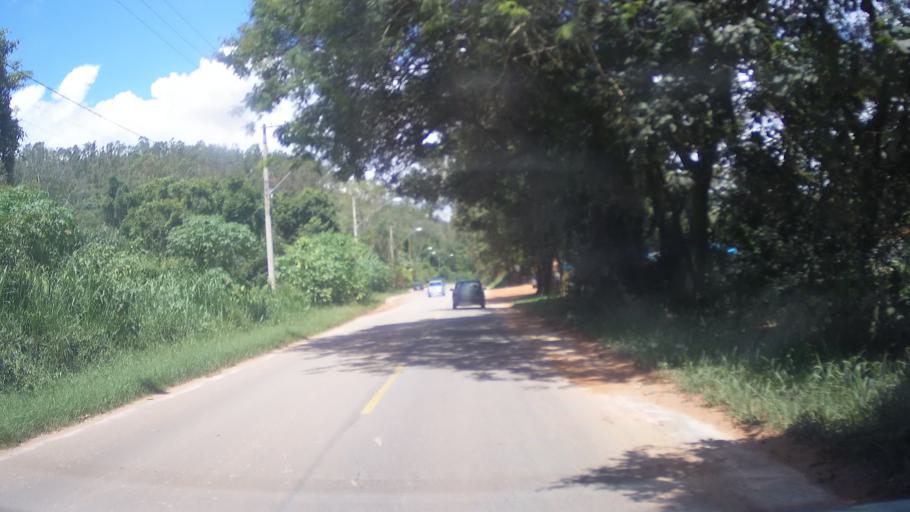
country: BR
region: Sao Paulo
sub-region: Campo Limpo Paulista
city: Campo Limpo Paulista
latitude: -23.2091
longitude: -46.7429
